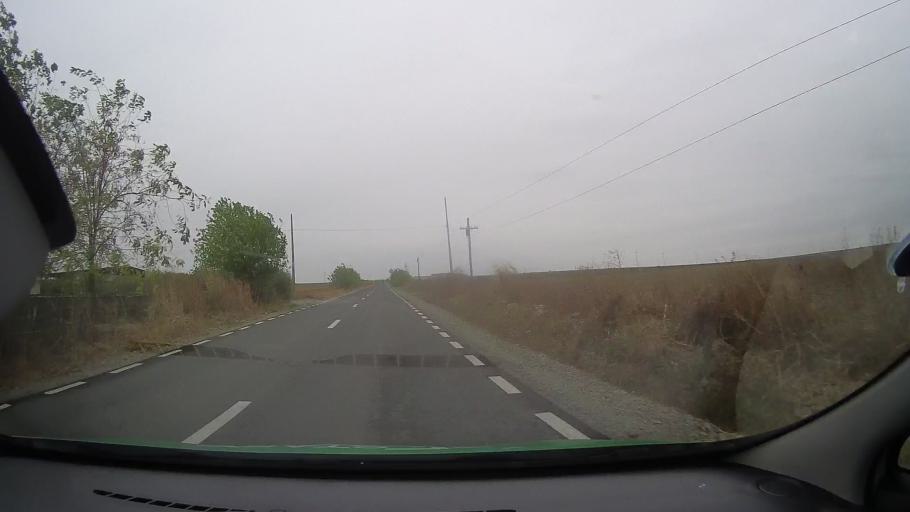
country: RO
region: Constanta
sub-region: Comuna Tortoman
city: Tortoman
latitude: 44.3639
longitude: 28.2091
